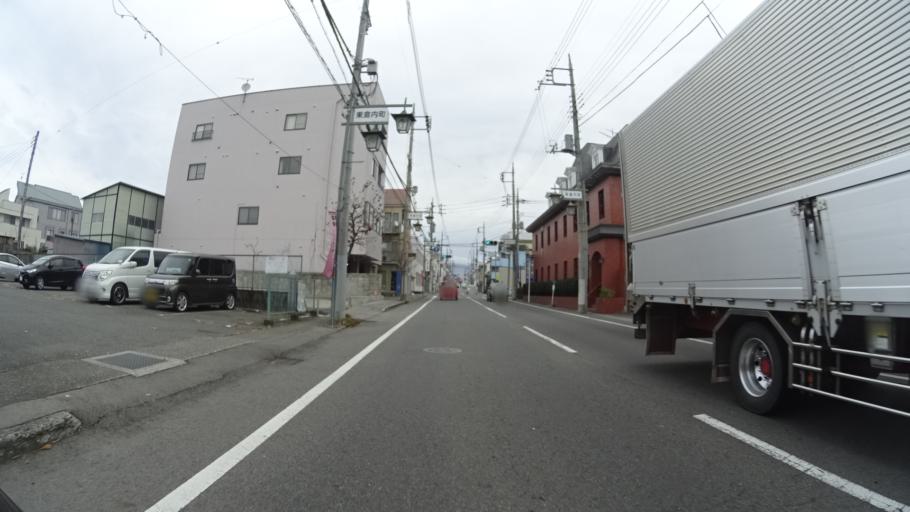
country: JP
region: Gunma
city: Numata
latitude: 36.6461
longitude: 139.0457
